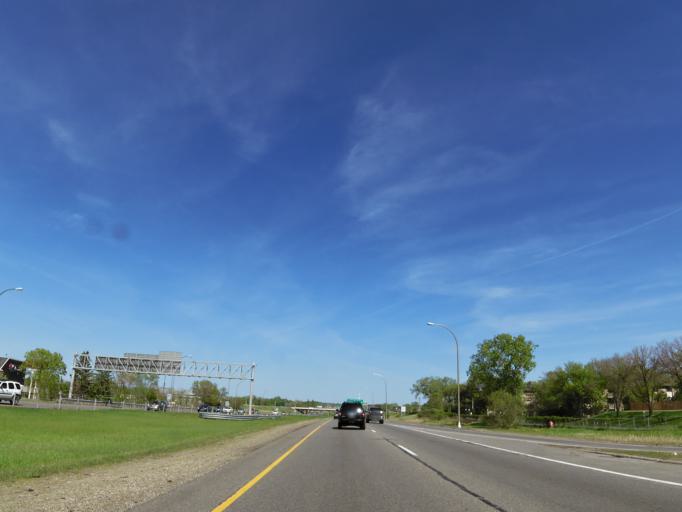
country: US
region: Minnesota
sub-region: Ramsey County
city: Roseville
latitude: 45.0101
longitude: -93.1734
